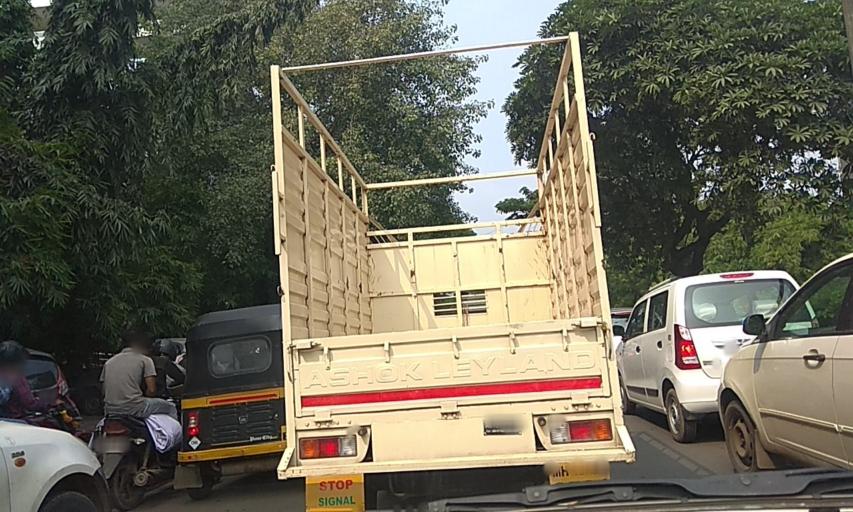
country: IN
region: Maharashtra
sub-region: Pune Division
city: Khadki
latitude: 18.5526
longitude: 73.8919
